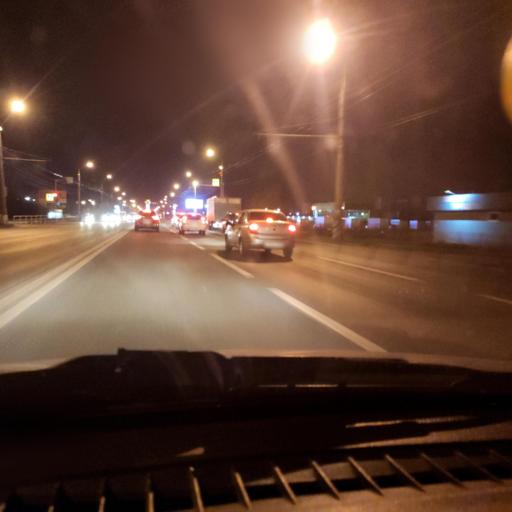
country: RU
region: Samara
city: Tol'yatti
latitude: 53.5501
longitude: 49.3250
